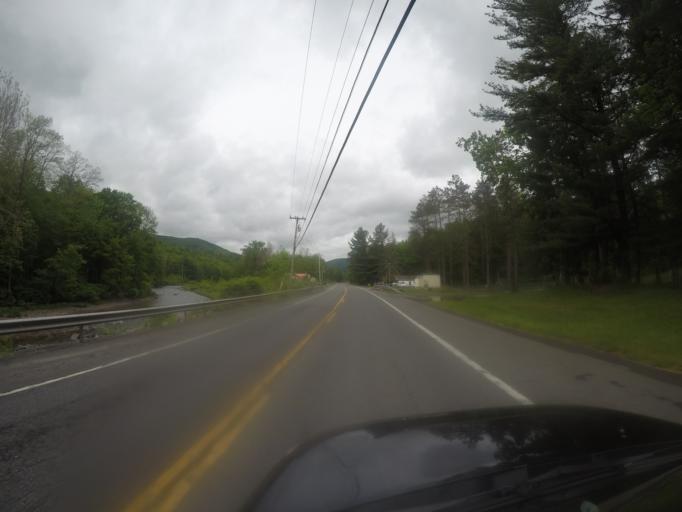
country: US
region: New York
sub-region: Ulster County
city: Shokan
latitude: 42.1146
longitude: -74.3631
